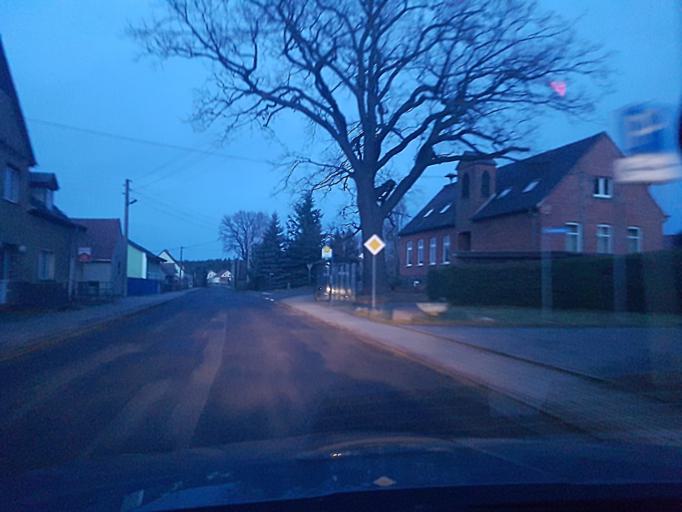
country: DE
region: Brandenburg
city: Bad Liebenwerda
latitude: 51.5449
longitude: 13.4207
